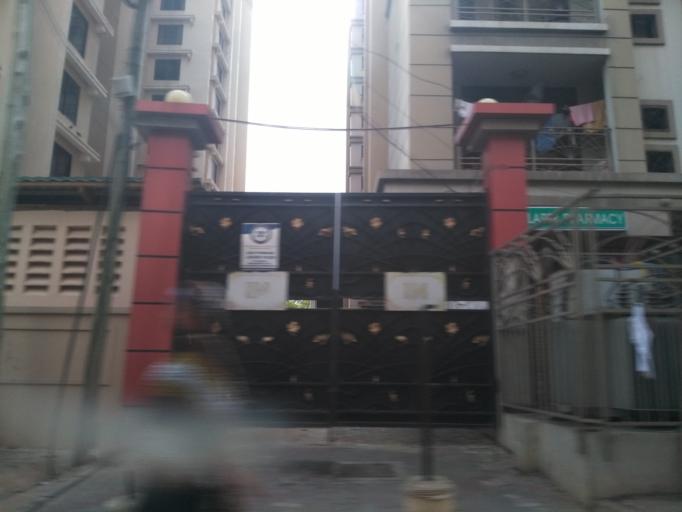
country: TZ
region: Dar es Salaam
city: Dar es Salaam
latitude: -6.8024
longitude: 39.2757
